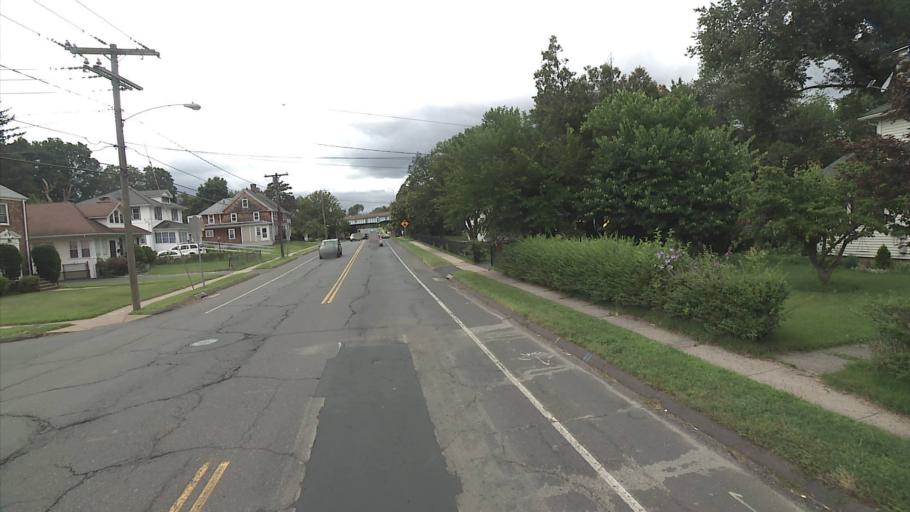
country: US
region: Connecticut
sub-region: Hartford County
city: Wethersfield
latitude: 41.7234
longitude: -72.6709
